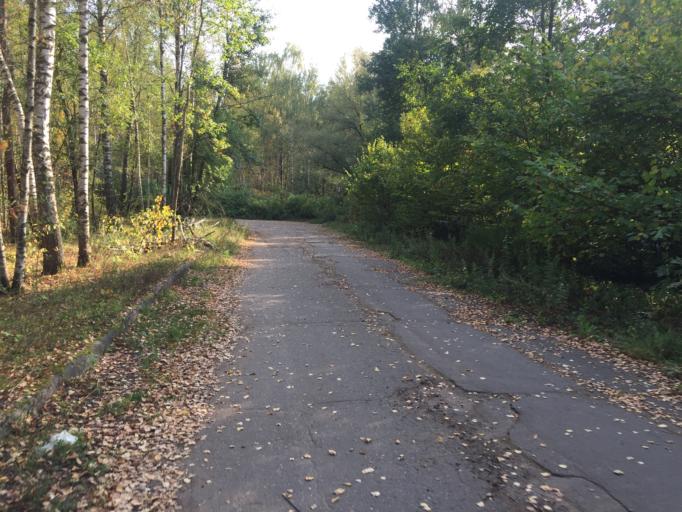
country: RU
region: Moscow
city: Babushkin
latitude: 55.8471
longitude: 37.7197
